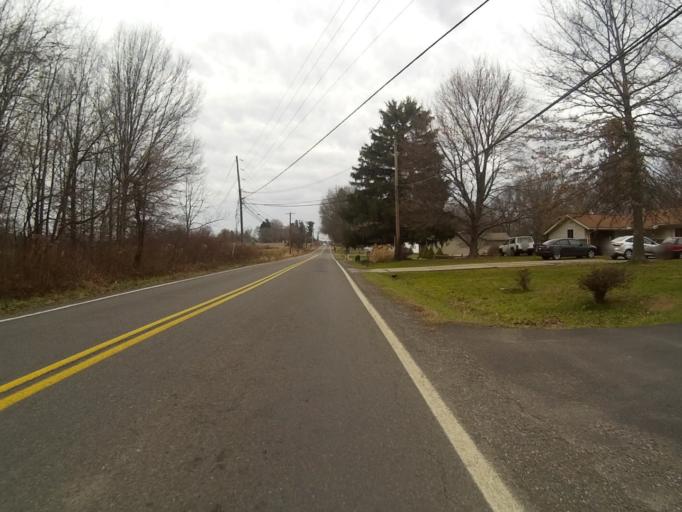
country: US
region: Ohio
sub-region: Portage County
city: Brimfield
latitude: 41.0828
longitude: -81.3416
